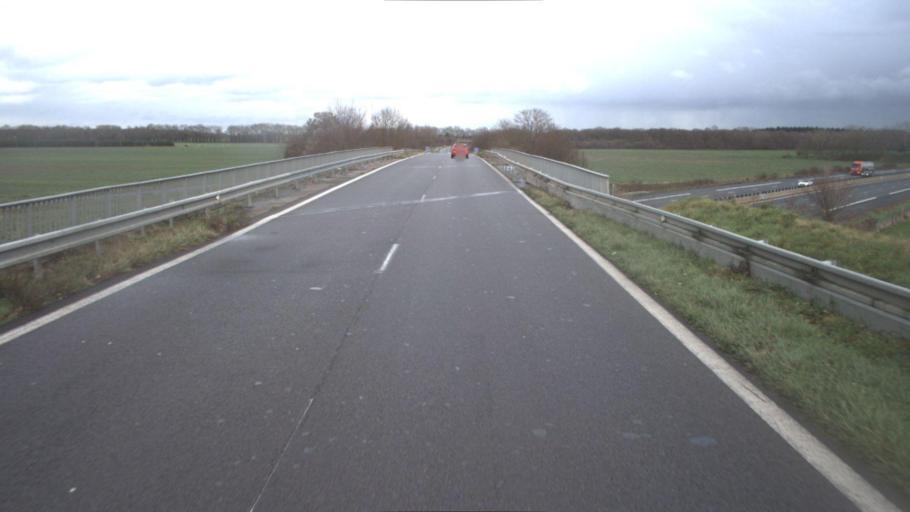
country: FR
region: Ile-de-France
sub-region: Departement de l'Essonne
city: Le Coudray-Montceaux
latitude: 48.5578
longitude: 2.4891
